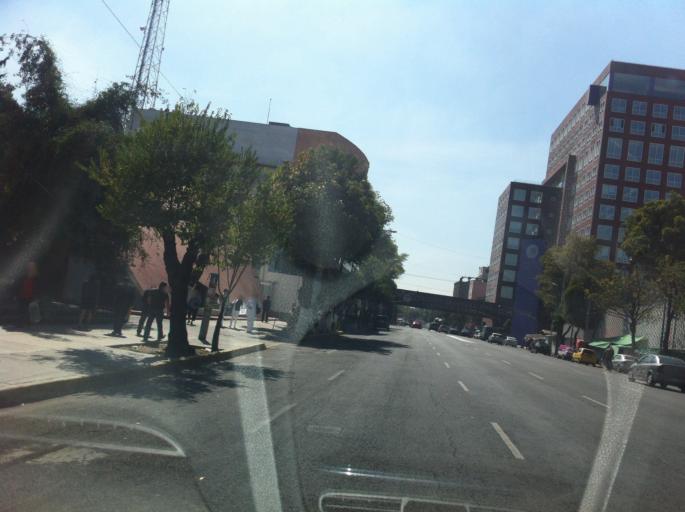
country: MX
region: Mexico City
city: Cuauhtemoc
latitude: 19.4234
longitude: -99.1496
